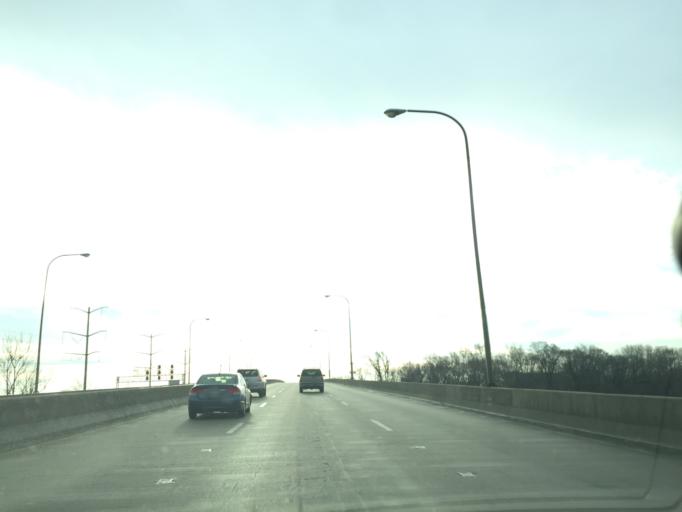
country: US
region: Illinois
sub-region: Cook County
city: Chicago
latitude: 41.7582
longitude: -87.5977
